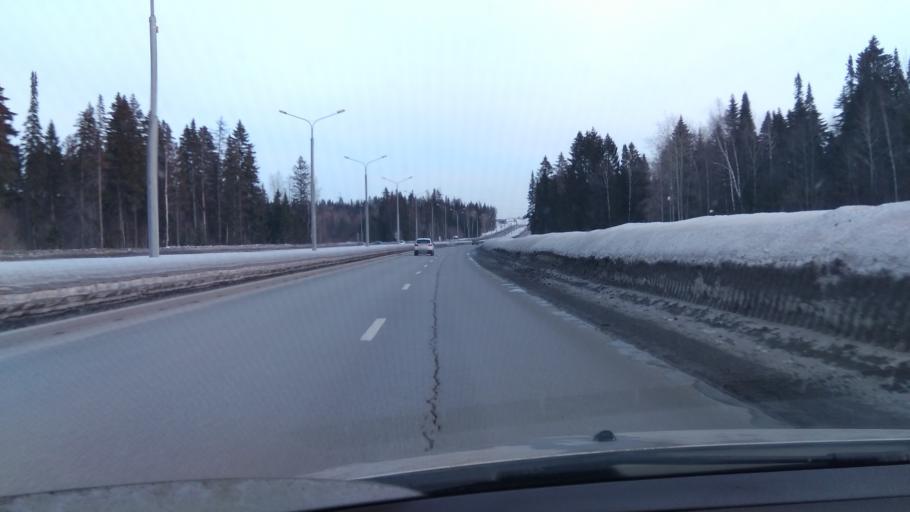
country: RU
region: Perm
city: Perm
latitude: 58.0044
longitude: 56.3684
